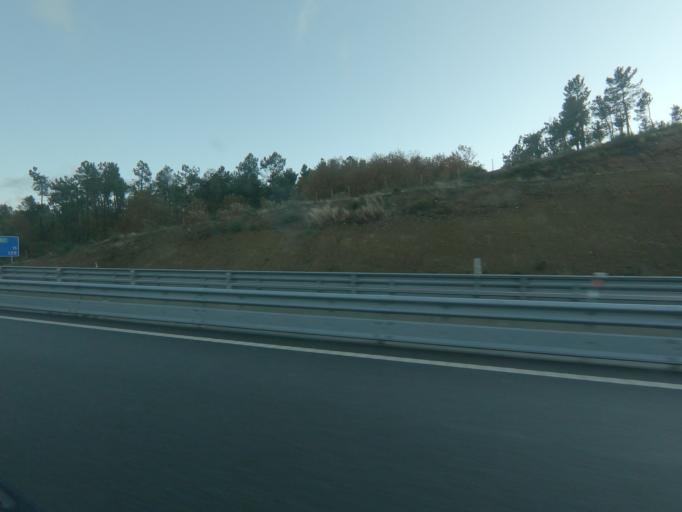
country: PT
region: Vila Real
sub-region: Santa Marta de Penaguiao
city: Santa Marta de Penaguiao
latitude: 41.2775
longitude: -7.8292
